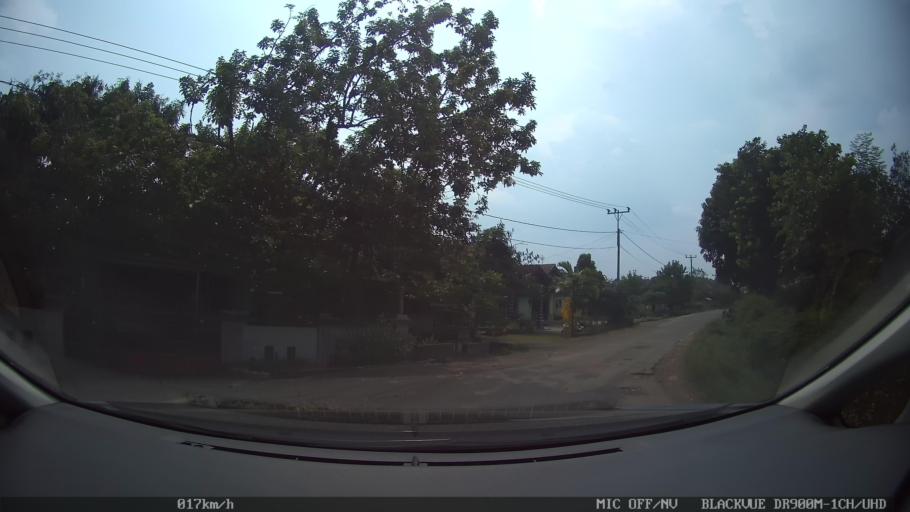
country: ID
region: Lampung
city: Gadingrejo
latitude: -5.3623
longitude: 105.0435
